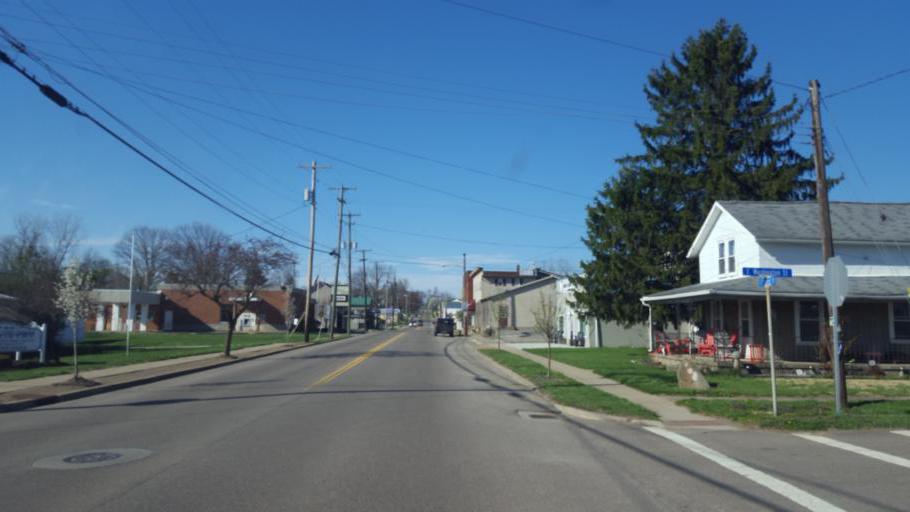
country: US
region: Ohio
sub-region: Knox County
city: Danville
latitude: 40.4432
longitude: -82.2606
